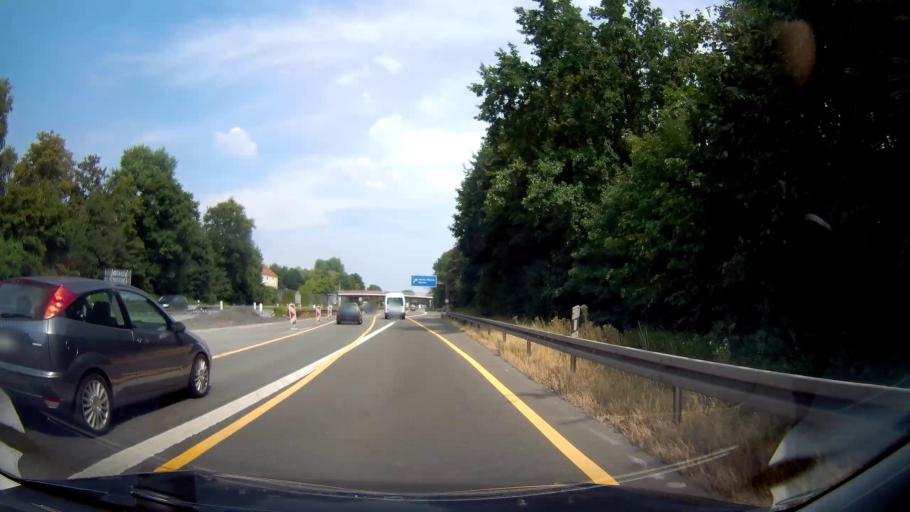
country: DE
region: North Rhine-Westphalia
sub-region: Regierungsbezirk Munster
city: Gelsenkirchen
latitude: 51.5394
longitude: 7.1437
